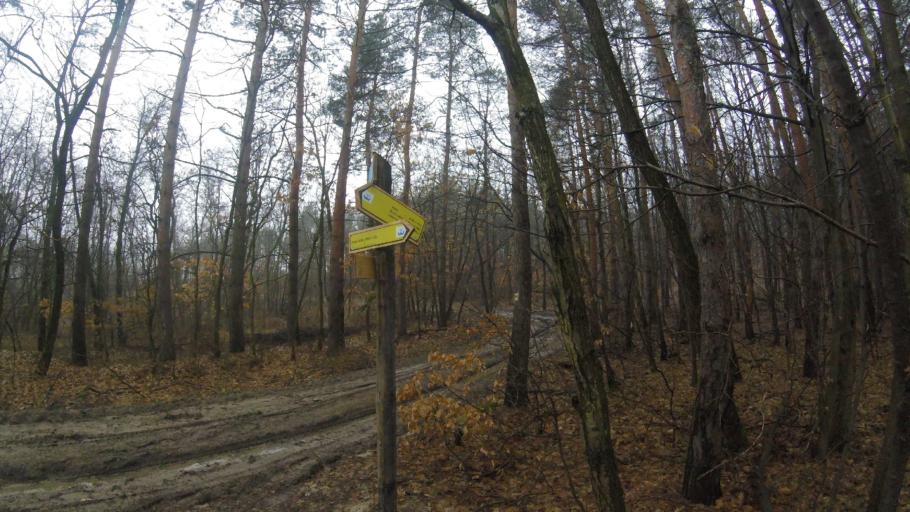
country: HU
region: Borsod-Abauj-Zemplen
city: Saly
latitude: 47.9666
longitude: 20.6188
